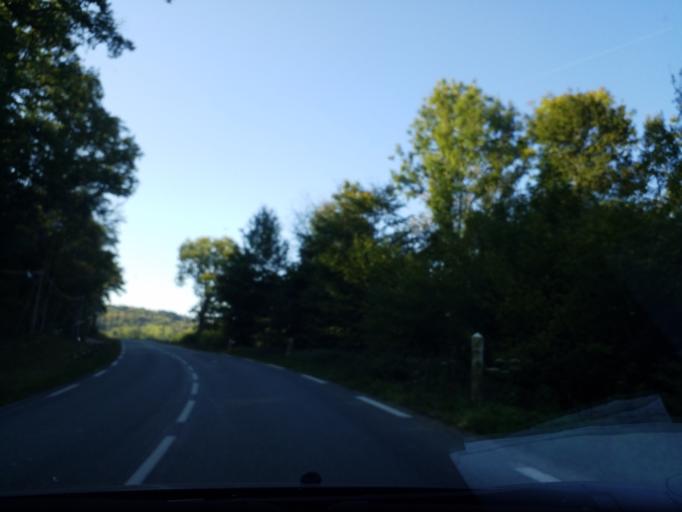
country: FR
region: Franche-Comte
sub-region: Departement du Doubs
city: Vercel-Villedieu-le-Camp
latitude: 47.2262
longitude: 6.3903
